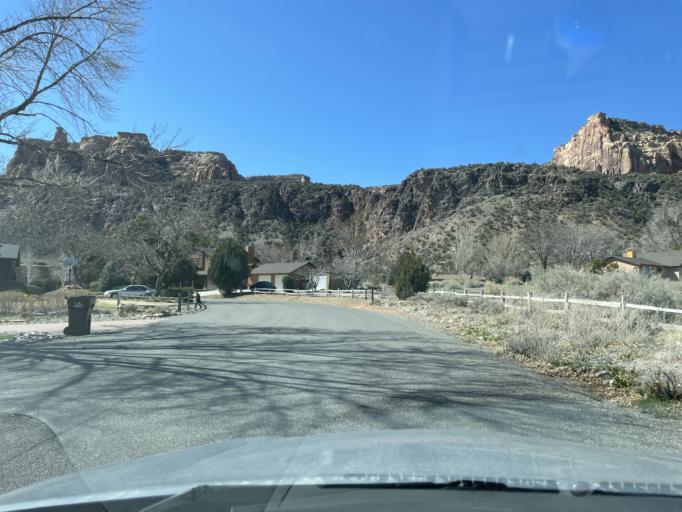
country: US
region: Colorado
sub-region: Mesa County
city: Redlands
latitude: 39.0797
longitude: -108.6761
